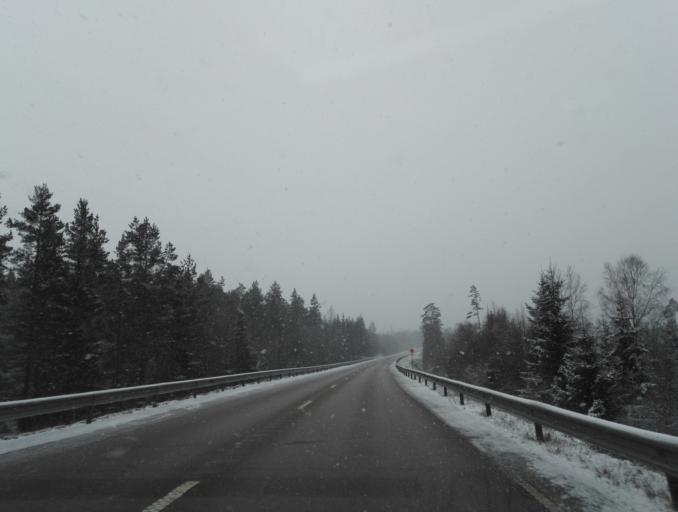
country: SE
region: Kronoberg
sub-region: Uppvidinge Kommun
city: Lenhovda
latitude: 57.0978
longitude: 15.2021
